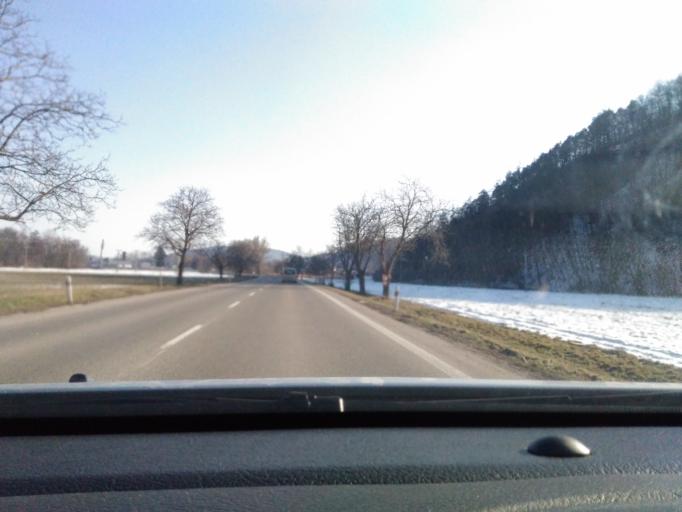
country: CZ
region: South Moravian
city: Predklasteri
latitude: 49.3467
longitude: 16.4120
